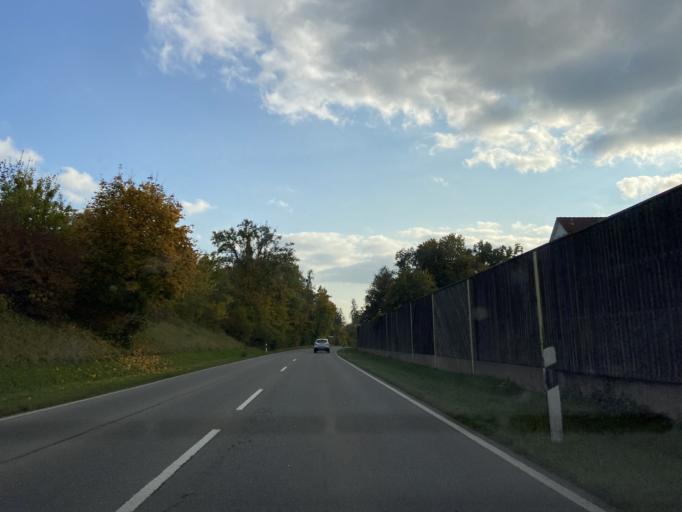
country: DE
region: Baden-Wuerttemberg
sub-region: Tuebingen Region
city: Sigmaringen
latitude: 48.0897
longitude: 9.2413
